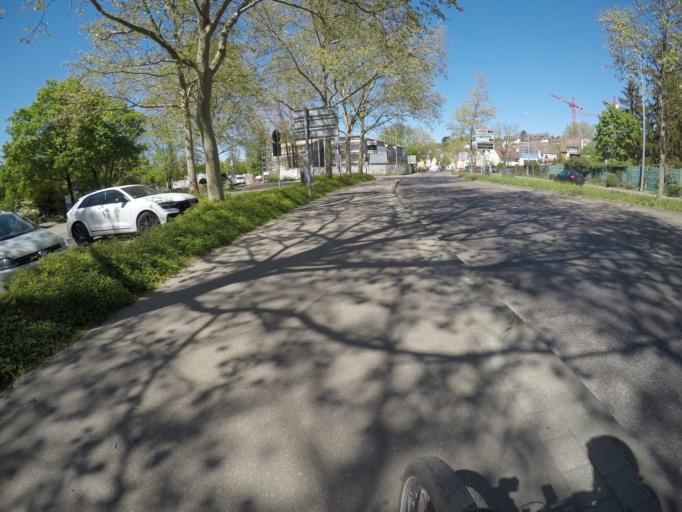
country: DE
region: Baden-Wuerttemberg
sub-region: Regierungsbezirk Stuttgart
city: Waiblingen
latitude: 48.8323
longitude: 9.3213
